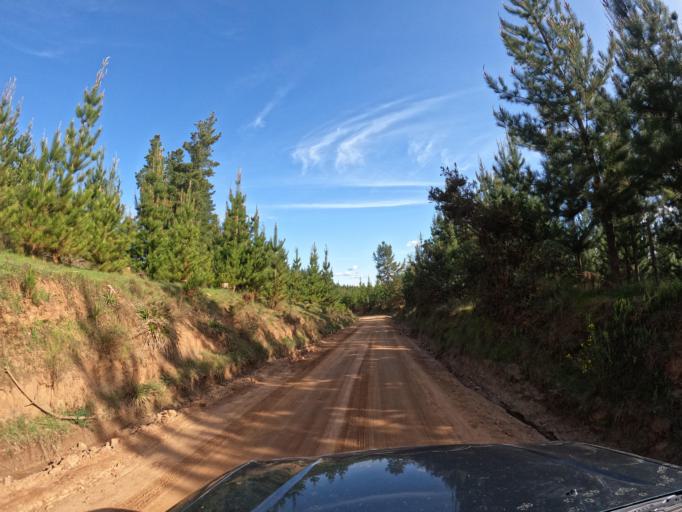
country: CL
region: Biobio
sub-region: Provincia de Biobio
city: Yumbel
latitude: -37.1011
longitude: -72.7410
